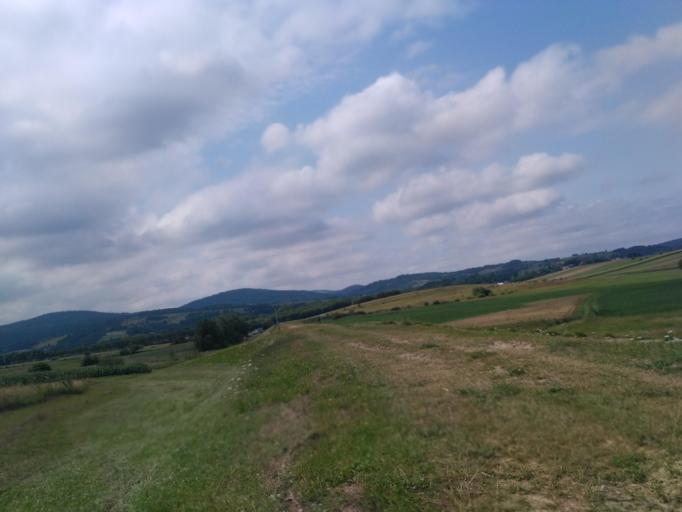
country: PL
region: Subcarpathian Voivodeship
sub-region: Powiat krosnienski
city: Rymanow
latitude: 49.5970
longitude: 21.8473
